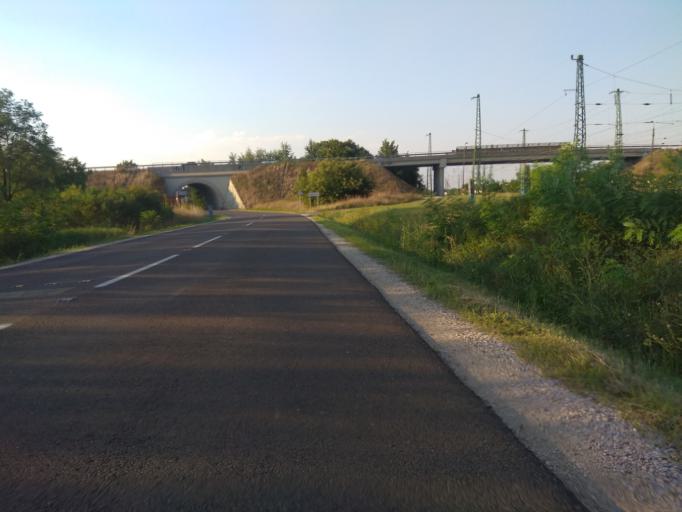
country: HU
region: Borsod-Abauj-Zemplen
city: Nyekladhaza
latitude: 47.9865
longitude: 20.8392
